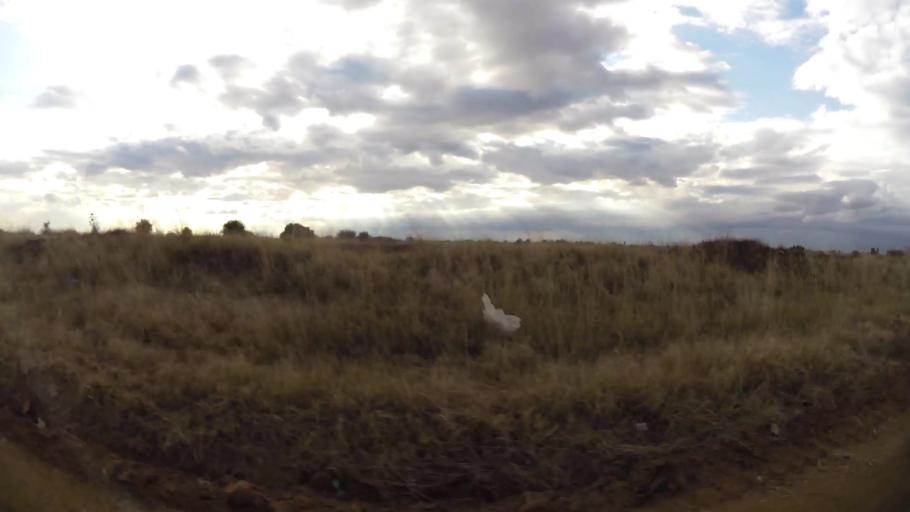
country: ZA
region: Orange Free State
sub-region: Lejweleputswa District Municipality
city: Welkom
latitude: -28.0102
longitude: 26.7274
